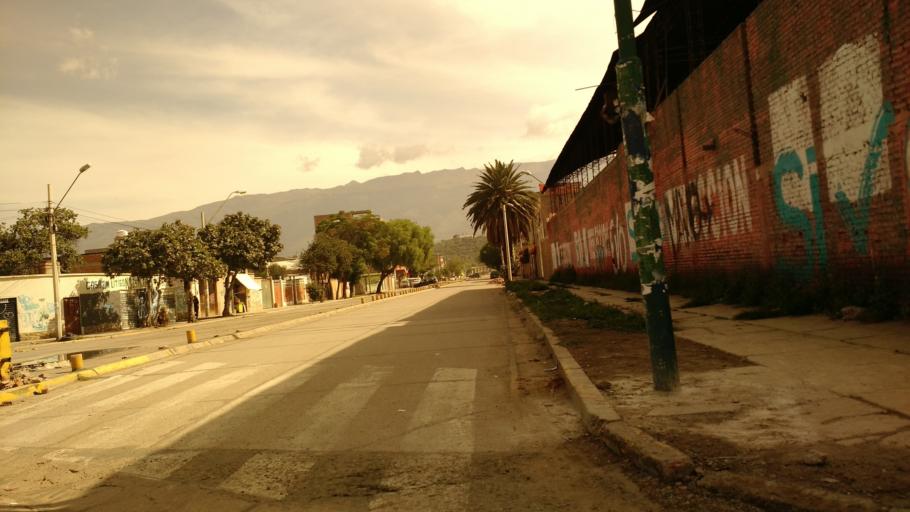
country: BO
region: Cochabamba
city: Cochabamba
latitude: -17.4185
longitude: -66.1596
